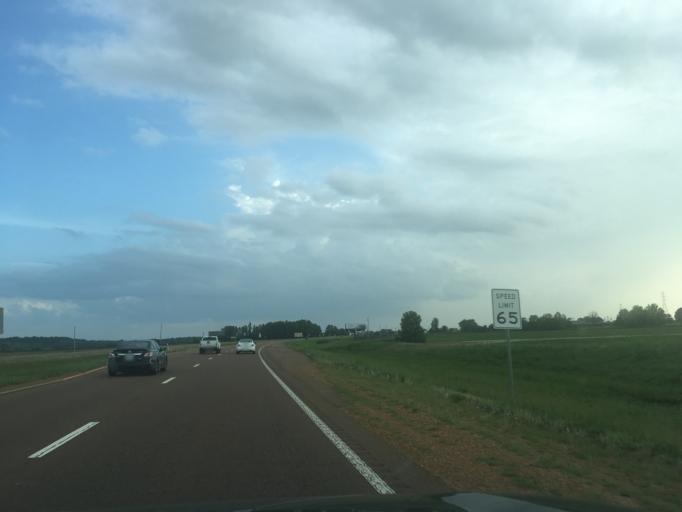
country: US
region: Mississippi
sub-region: De Soto County
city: Walls
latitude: 34.9543
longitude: -90.1430
